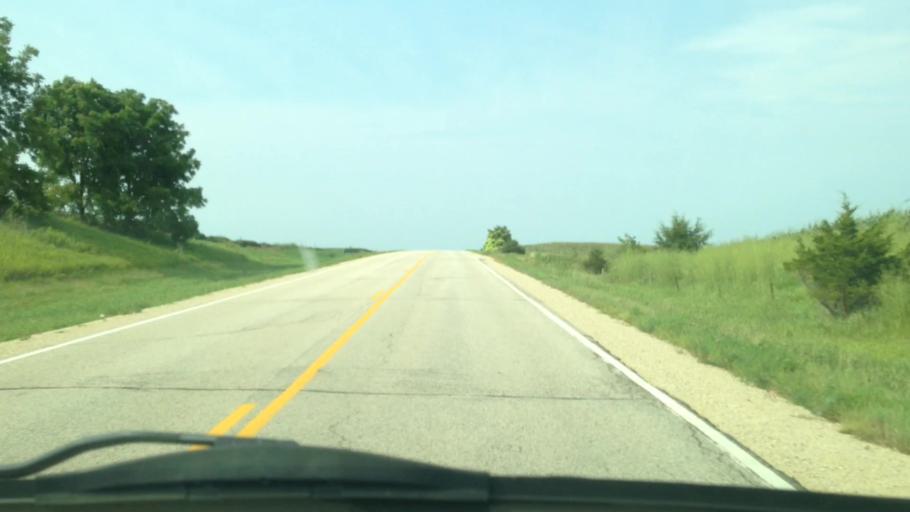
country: US
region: Minnesota
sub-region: Winona County
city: Saint Charles
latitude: 43.8676
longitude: -91.9594
